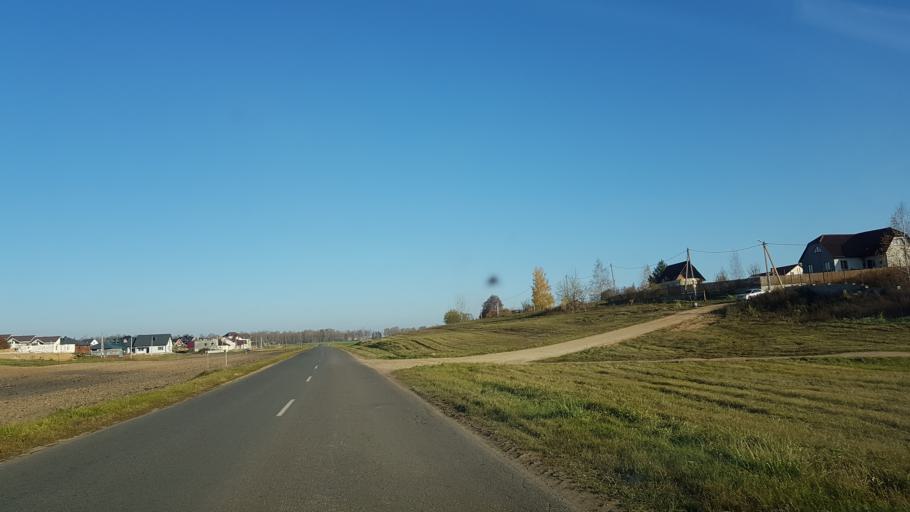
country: BY
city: Fanipol
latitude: 53.7245
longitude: 27.3172
